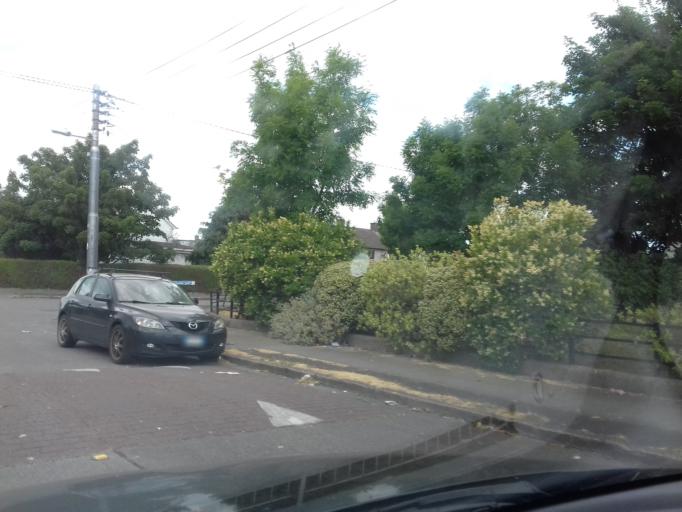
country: IE
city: Bonnybrook
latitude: 53.3974
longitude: -6.1993
